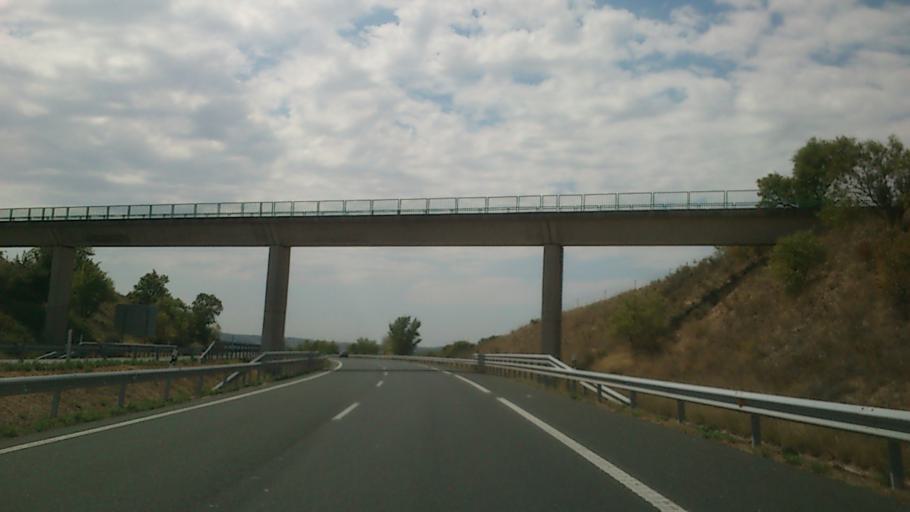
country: ES
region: La Rioja
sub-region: Provincia de La Rioja
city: Cenicero
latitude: 42.4790
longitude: -2.6589
